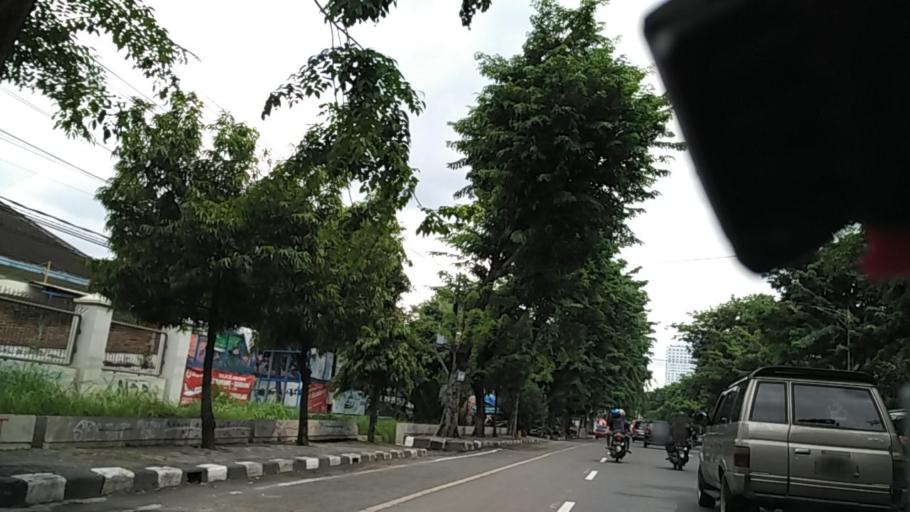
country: ID
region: Central Java
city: Semarang
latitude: -6.9974
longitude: 110.4337
